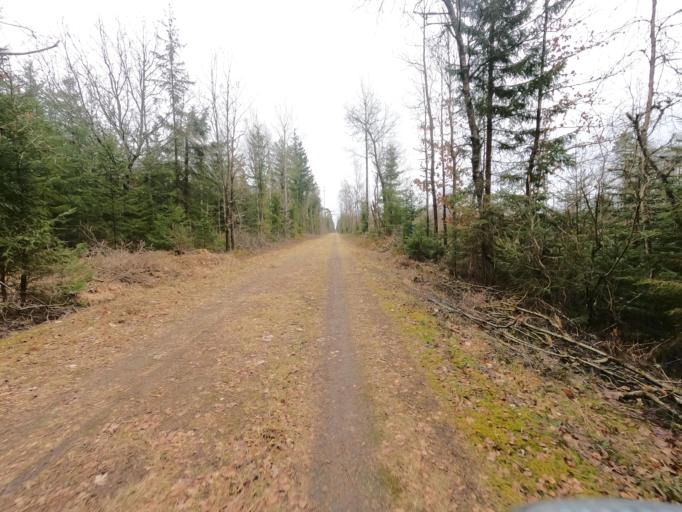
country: SE
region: Kronoberg
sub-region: Ljungby Kommun
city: Ljungby
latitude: 56.8228
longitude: 13.7259
